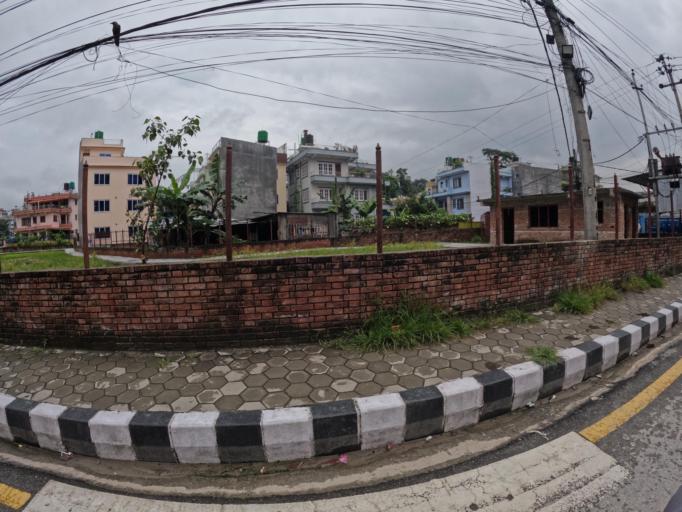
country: NP
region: Central Region
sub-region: Bagmati Zone
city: Kathmandu
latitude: 27.7555
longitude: 85.3253
